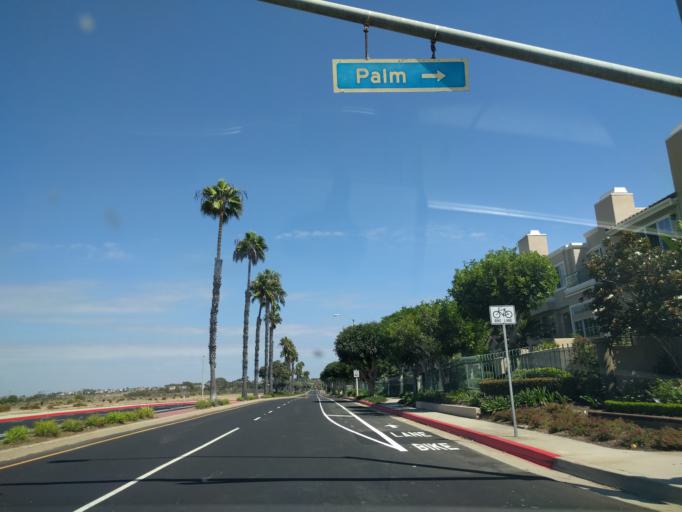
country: US
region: California
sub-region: Orange County
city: Huntington Beach
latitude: 33.6816
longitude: -118.0287
